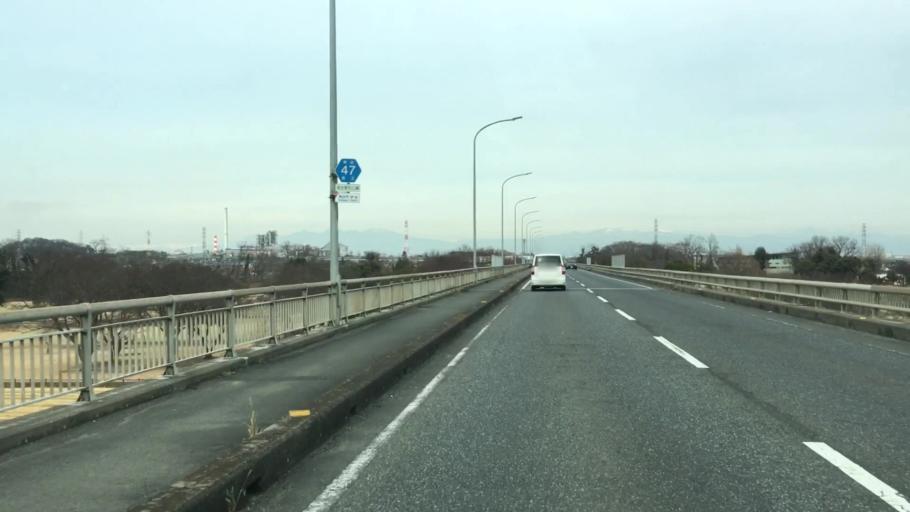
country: JP
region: Saitama
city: Kumagaya
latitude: 36.1395
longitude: 139.3232
